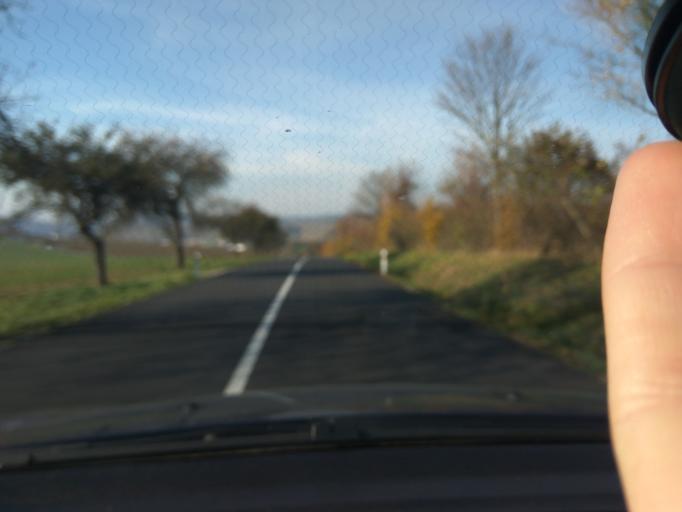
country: SK
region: Nitriansky
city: Brezova pod Bradlom
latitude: 48.6713
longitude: 17.5580
